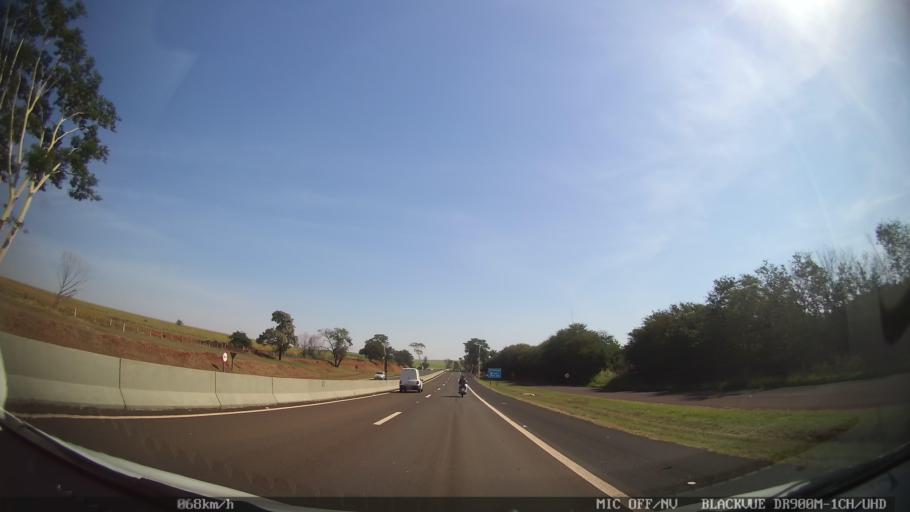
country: BR
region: Sao Paulo
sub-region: Ribeirao Preto
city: Ribeirao Preto
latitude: -21.1669
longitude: -47.8728
